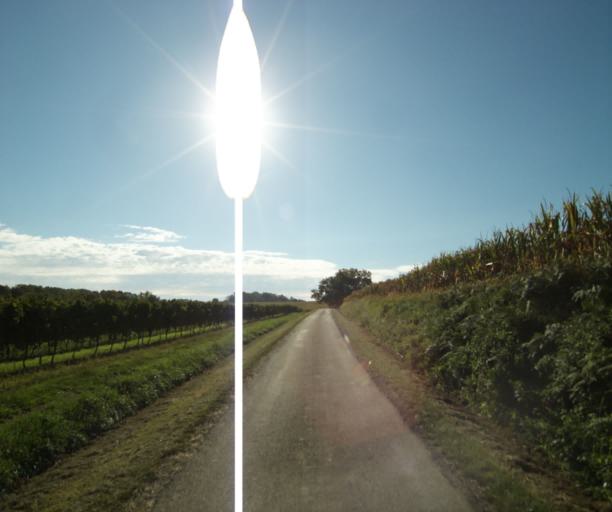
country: FR
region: Aquitaine
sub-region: Departement des Landes
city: Gabarret
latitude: 43.9096
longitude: 0.0063
